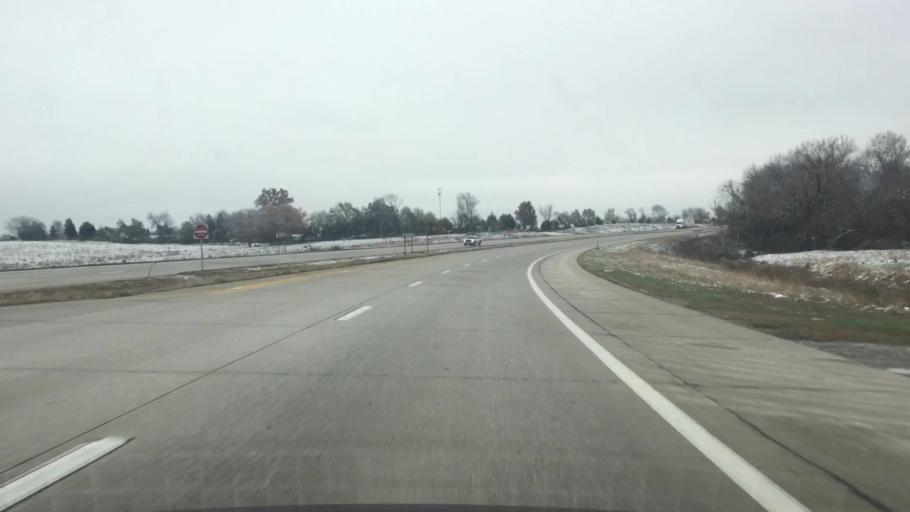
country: US
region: Missouri
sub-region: Saint Clair County
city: Osceola
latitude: 38.1759
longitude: -93.7225
